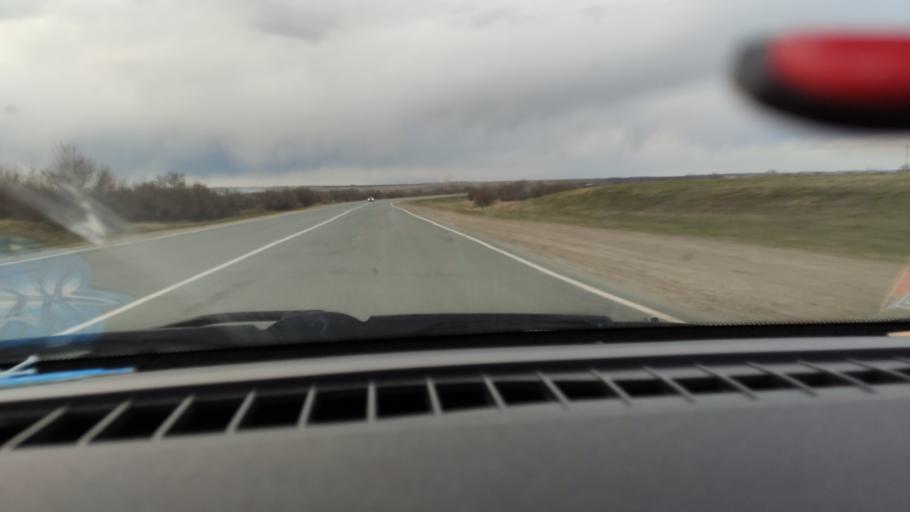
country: RU
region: Saratov
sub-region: Saratovskiy Rayon
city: Saratov
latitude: 51.7241
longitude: 46.0281
